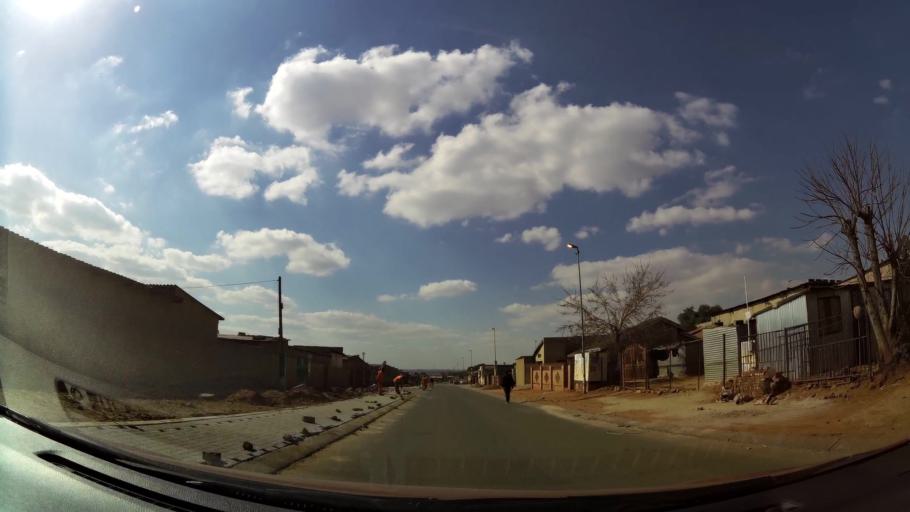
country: ZA
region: Gauteng
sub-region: Ekurhuleni Metropolitan Municipality
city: Tembisa
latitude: -26.0040
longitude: 28.2170
